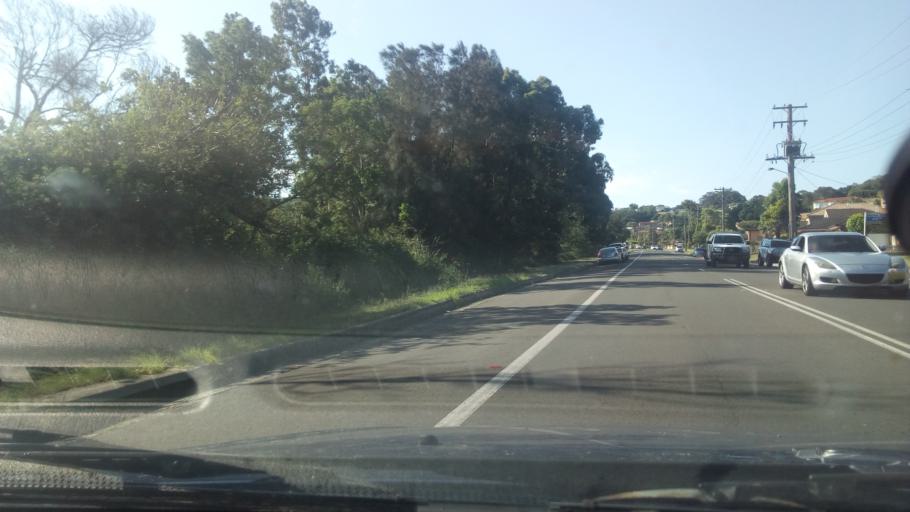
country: AU
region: New South Wales
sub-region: Wollongong
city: Berkeley
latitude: -34.4780
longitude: 150.8553
